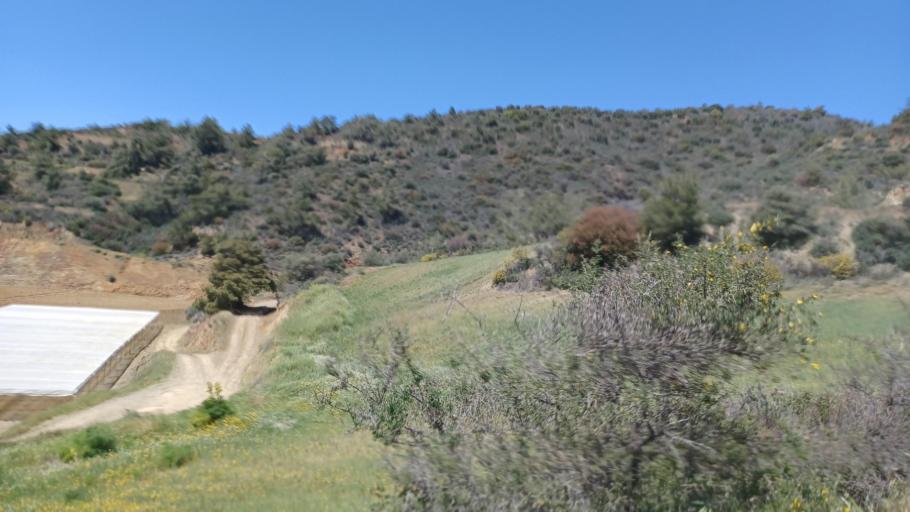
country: CY
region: Limassol
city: Parekklisha
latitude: 34.8189
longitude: 33.1448
